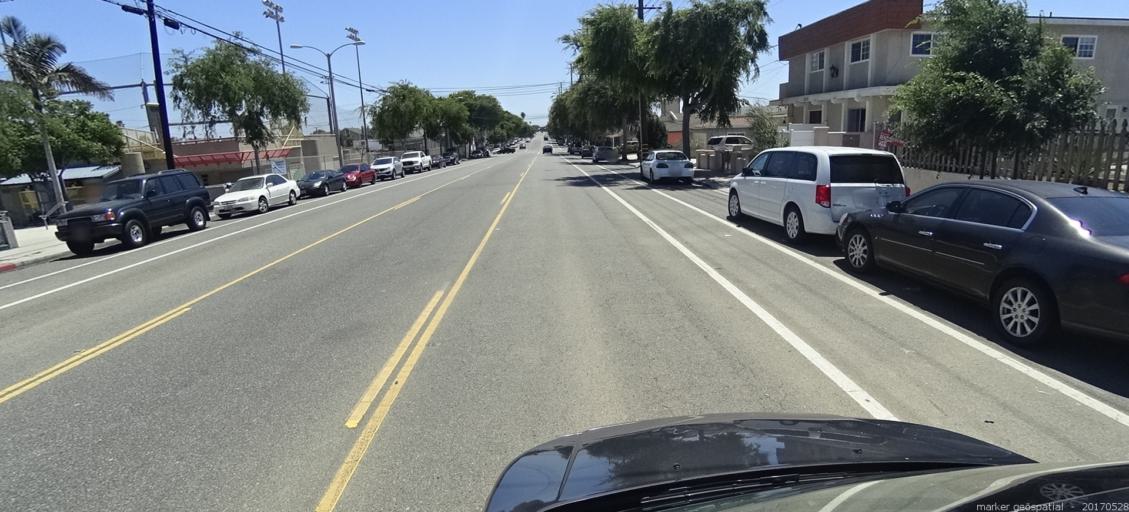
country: US
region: California
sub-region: Los Angeles County
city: Lawndale
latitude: 33.8690
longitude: -118.3700
